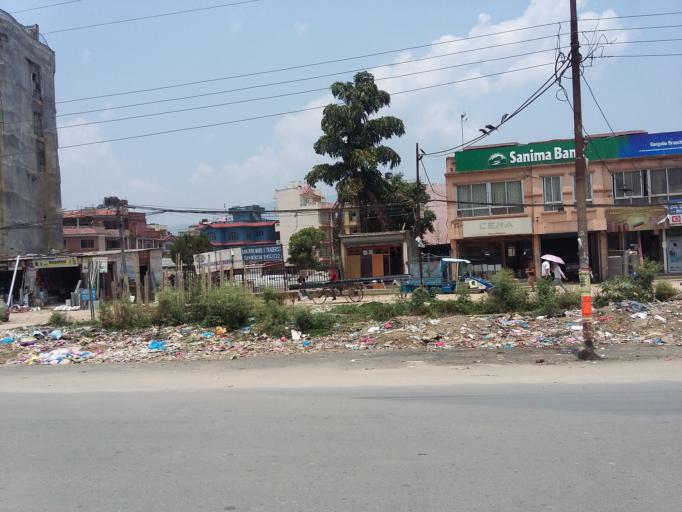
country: NP
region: Central Region
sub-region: Bagmati Zone
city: Kathmandu
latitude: 27.7351
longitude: 85.3167
